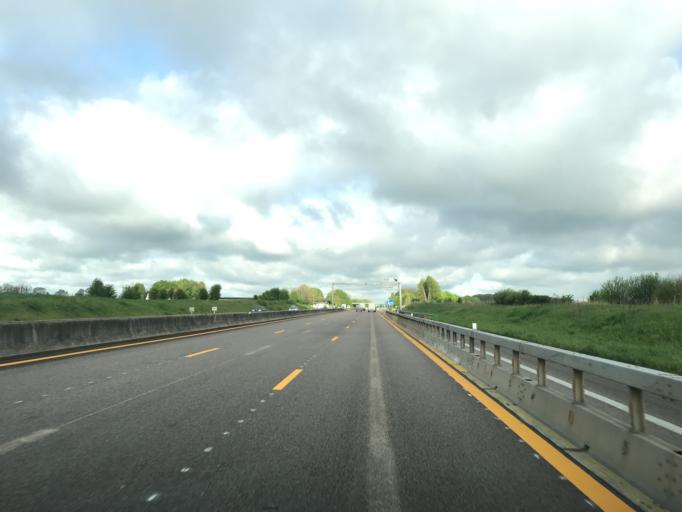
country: FR
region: Haute-Normandie
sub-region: Departement de l'Eure
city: Corneville-sur-Risle
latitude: 49.3767
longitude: 0.6323
